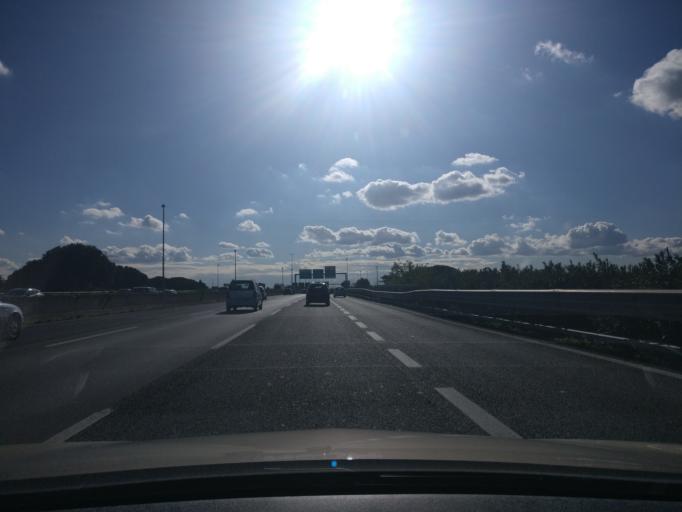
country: IT
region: Latium
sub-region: Citta metropolitana di Roma Capitale
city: Ciampino
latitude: 41.8391
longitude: 12.5910
